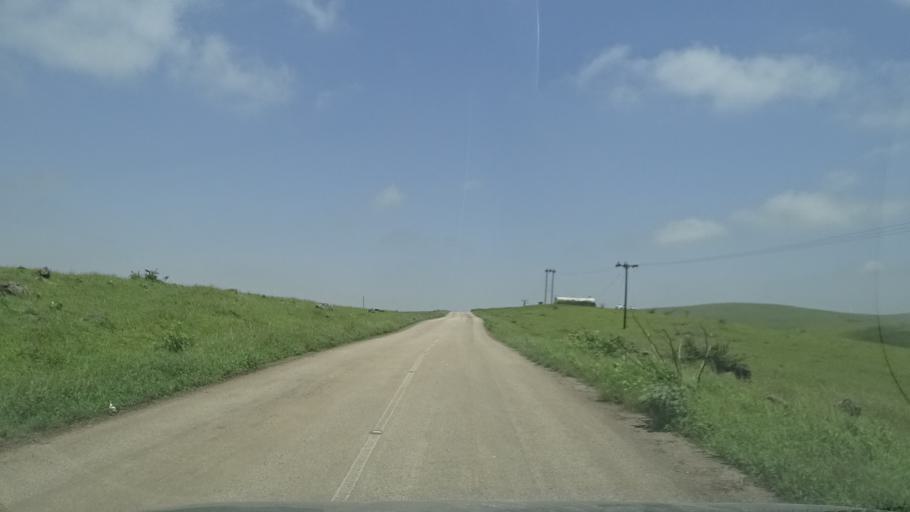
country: OM
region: Zufar
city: Salalah
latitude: 17.2338
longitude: 54.2164
